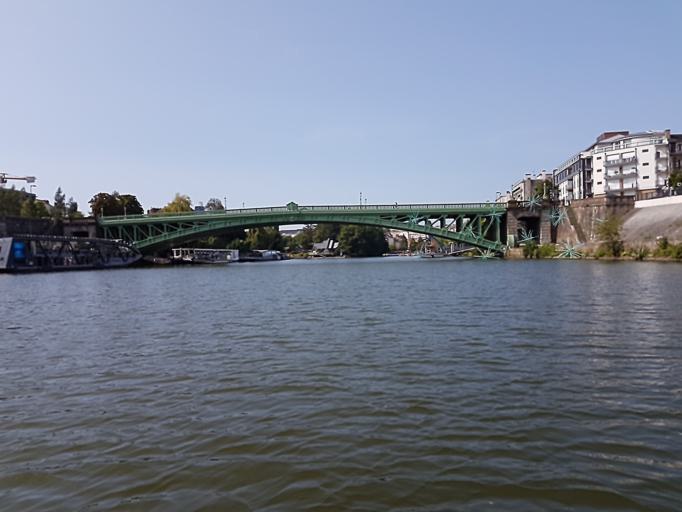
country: FR
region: Pays de la Loire
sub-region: Departement de la Loire-Atlantique
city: Nantes
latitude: 47.2290
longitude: -1.5518
